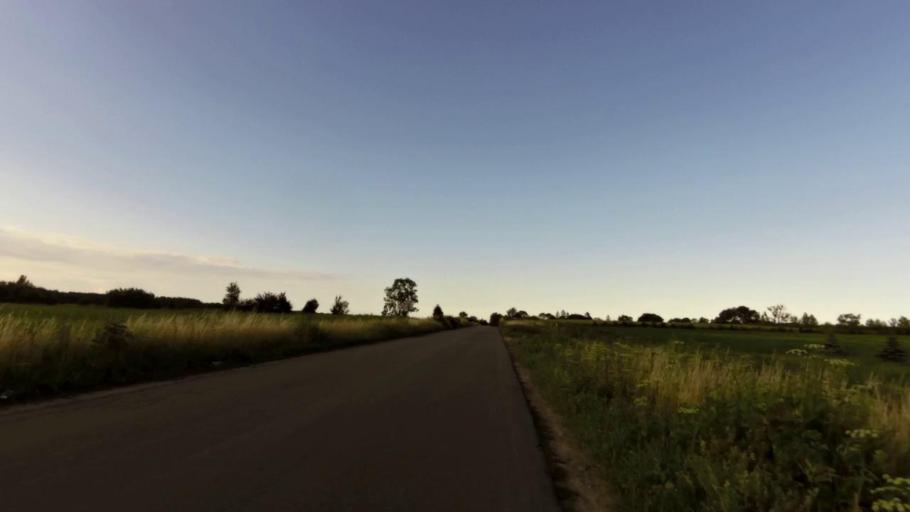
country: PL
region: West Pomeranian Voivodeship
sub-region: Powiat slawienski
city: Darlowo
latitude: 54.4005
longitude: 16.3645
